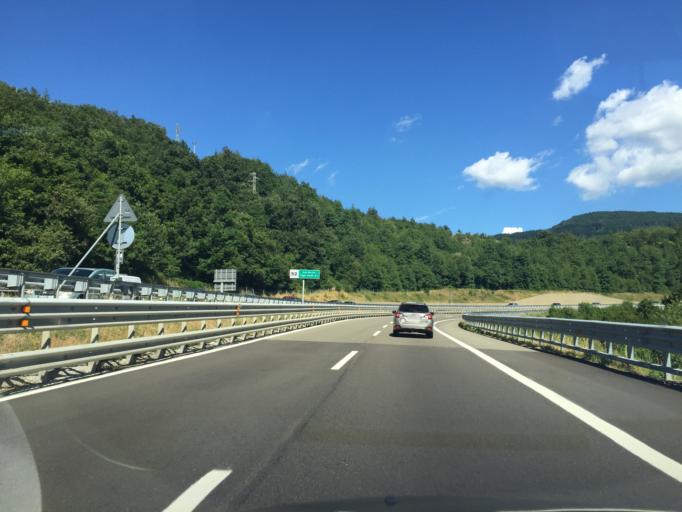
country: IT
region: Emilia-Romagna
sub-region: Provincia di Parma
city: Berceto
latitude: 44.5031
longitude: 9.9507
